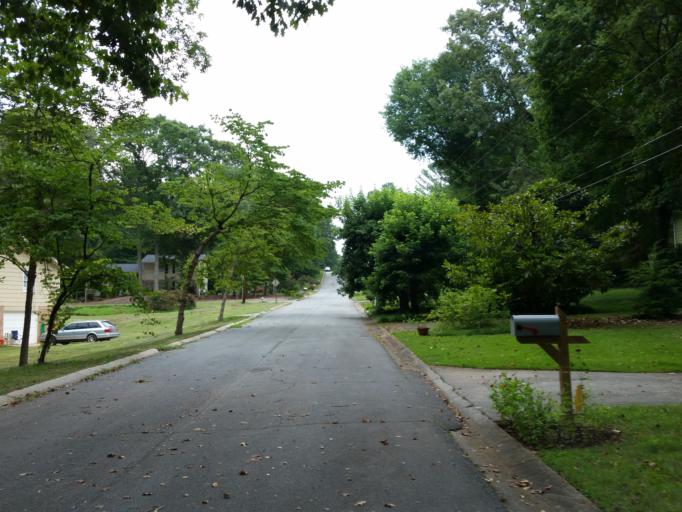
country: US
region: Georgia
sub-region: Cherokee County
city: Woodstock
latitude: 34.0200
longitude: -84.4778
